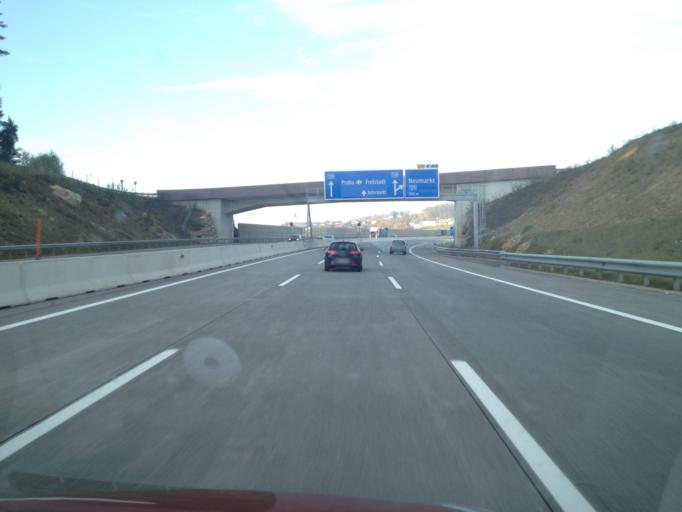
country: AT
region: Upper Austria
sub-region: Politischer Bezirk Urfahr-Umgebung
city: Alberndorf in der Riedmark
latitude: 48.4127
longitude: 14.4848
